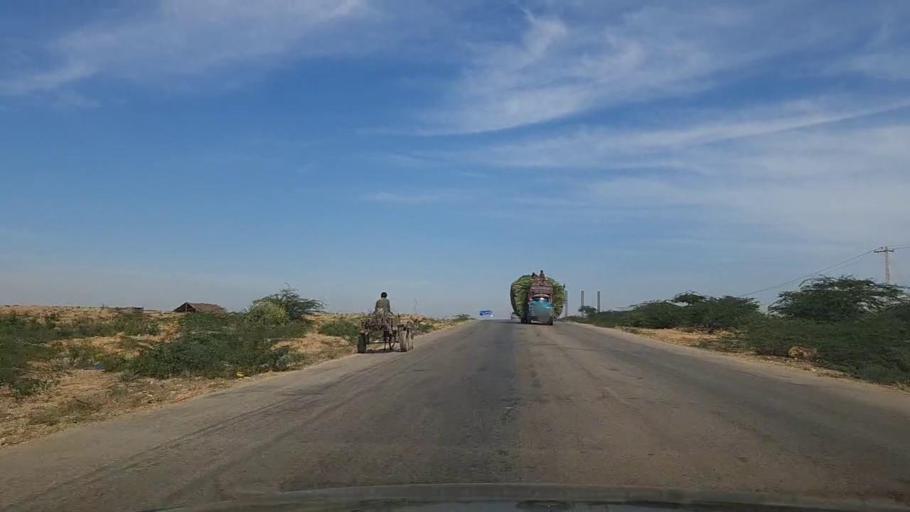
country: PK
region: Sindh
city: Bulri
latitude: 25.0403
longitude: 68.2405
